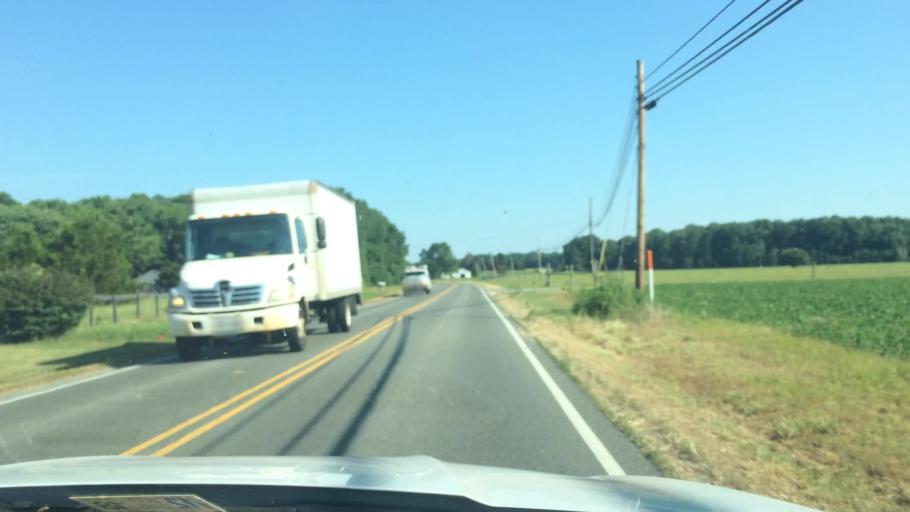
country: US
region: Virginia
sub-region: Lancaster County
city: Lancaster
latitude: 37.7920
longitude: -76.5188
